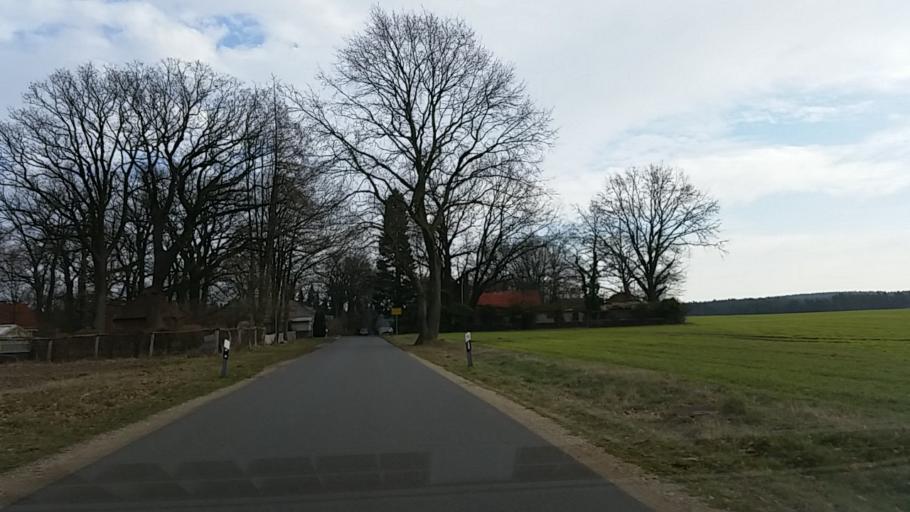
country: DE
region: Lower Saxony
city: Soltendieck
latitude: 52.8508
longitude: 10.7735
